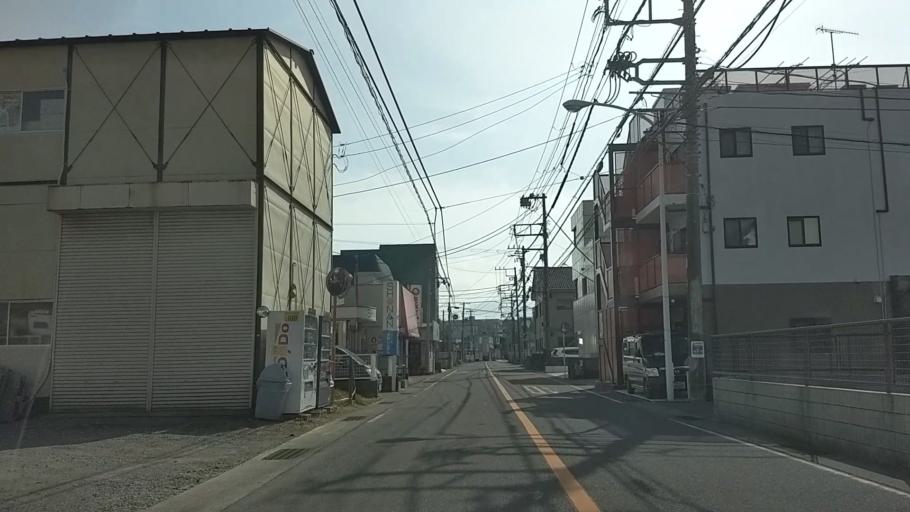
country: JP
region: Kanagawa
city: Chigasaki
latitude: 35.3374
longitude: 139.3829
